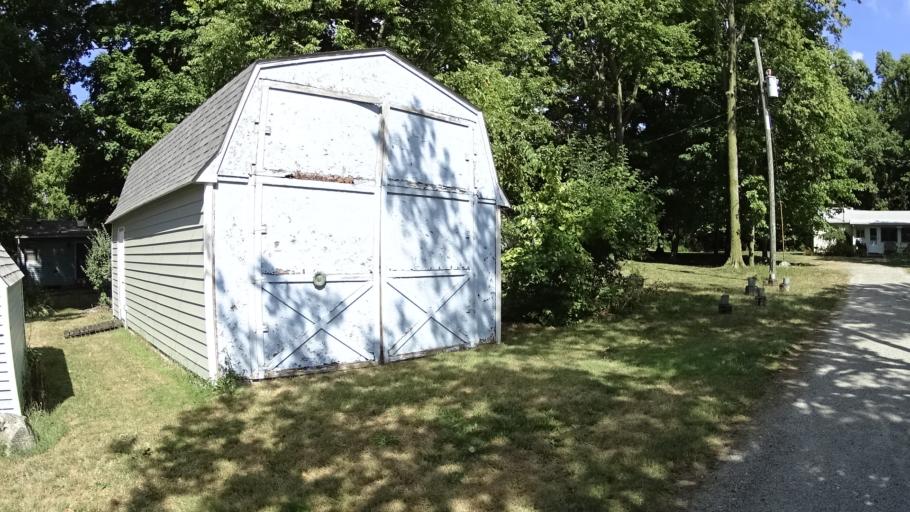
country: US
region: Ohio
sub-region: Erie County
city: Sandusky
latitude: 41.6008
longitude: -82.7290
